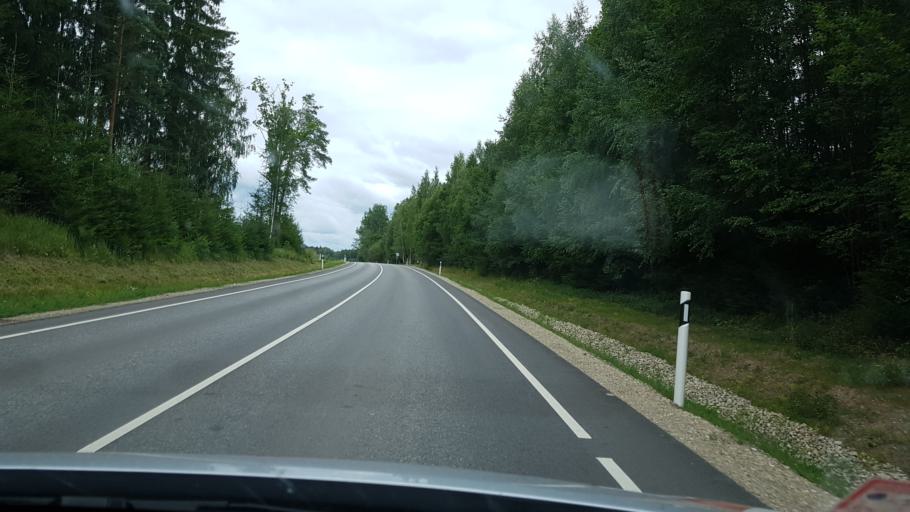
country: EE
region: Polvamaa
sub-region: Polva linn
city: Polva
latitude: 58.0227
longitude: 27.1630
